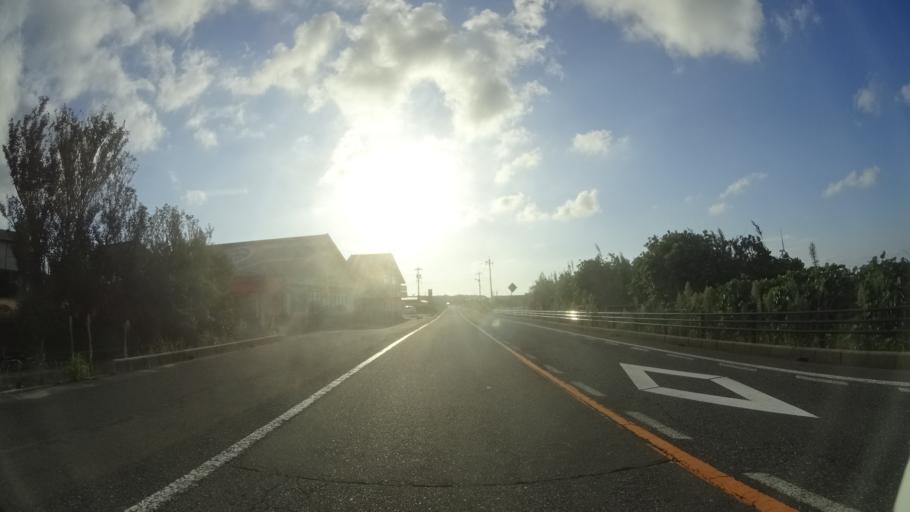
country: JP
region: Tottori
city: Yonago
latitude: 35.5204
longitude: 133.5654
